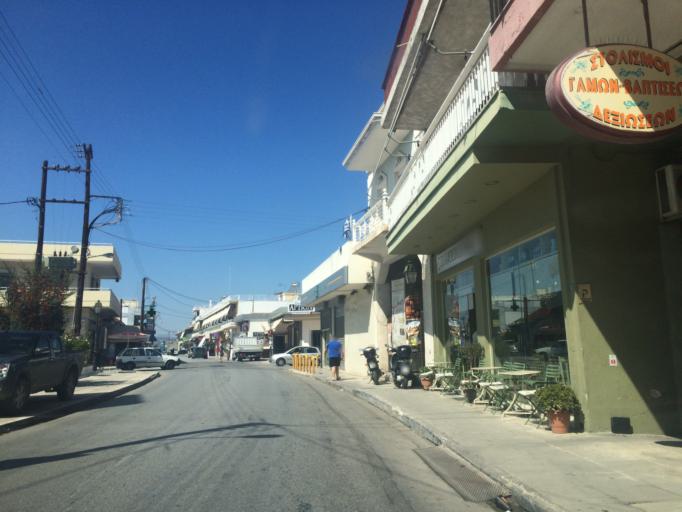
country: GR
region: Peloponnese
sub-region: Nomos Korinthias
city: Vrakhati
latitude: 37.9555
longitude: 22.8025
